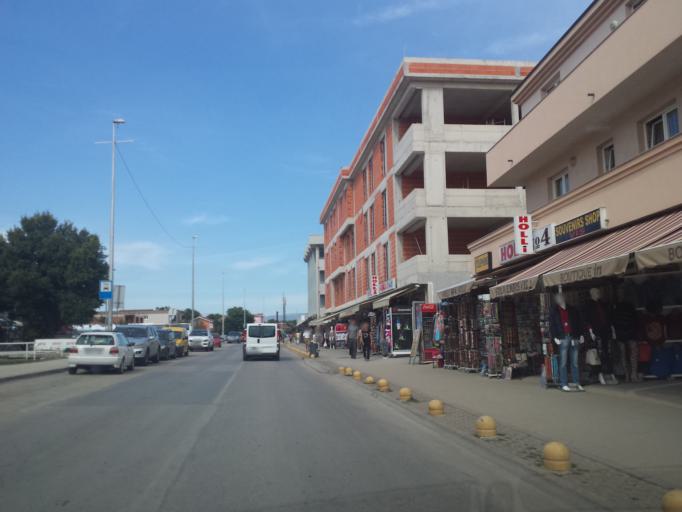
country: BA
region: Federation of Bosnia and Herzegovina
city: Citluk
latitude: 43.1921
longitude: 17.6783
